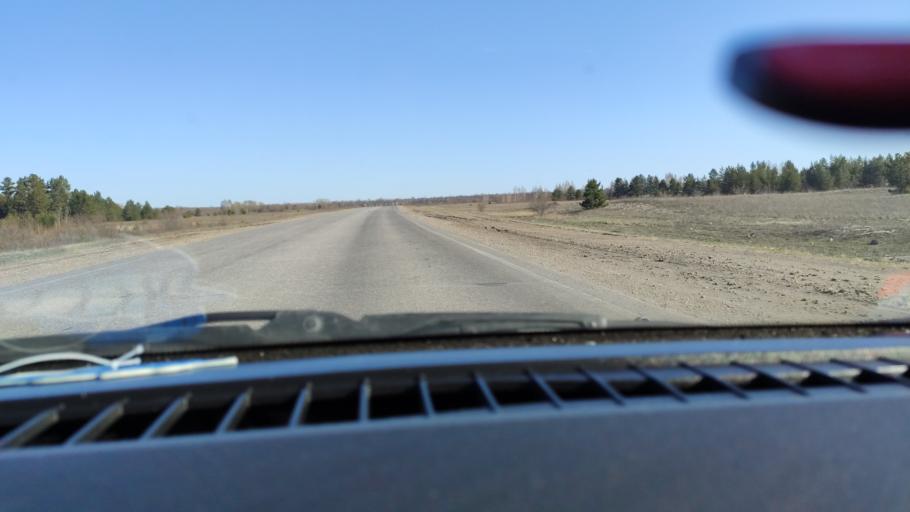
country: RU
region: Samara
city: Varlamovo
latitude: 53.1499
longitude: 48.2843
